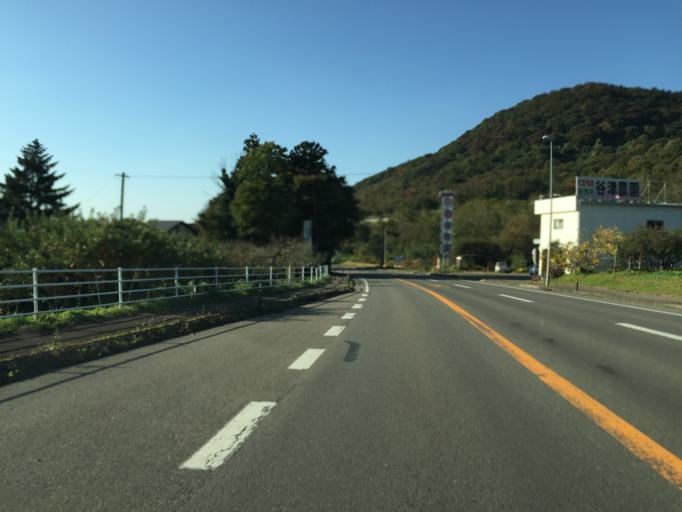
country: JP
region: Fukushima
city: Yanagawamachi-saiwaicho
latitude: 37.8981
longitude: 140.5713
